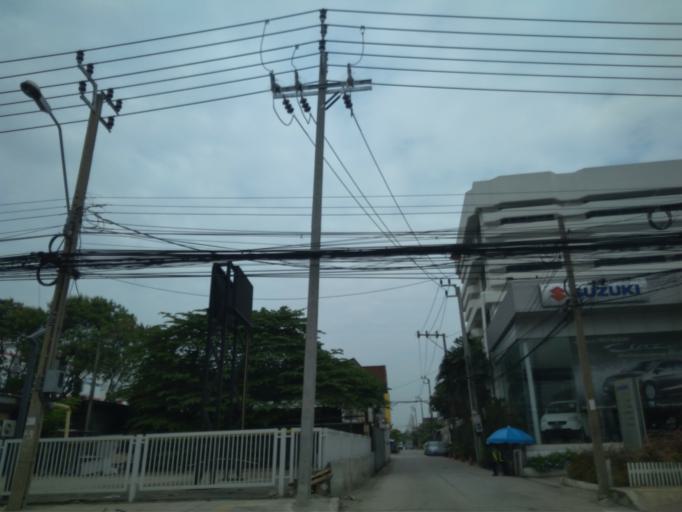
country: TH
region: Bangkok
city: Suan Luang
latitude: 13.7018
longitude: 100.6464
